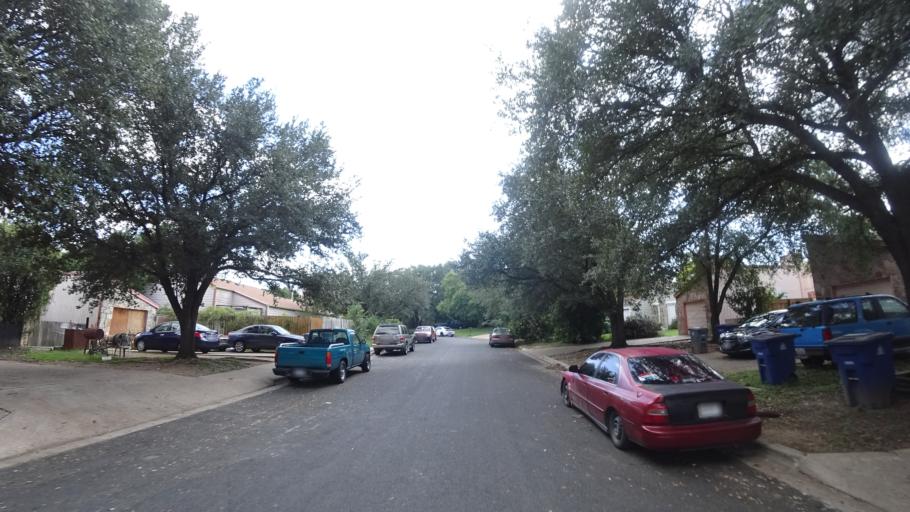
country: US
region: Texas
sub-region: Travis County
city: Onion Creek
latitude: 30.2039
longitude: -97.7901
